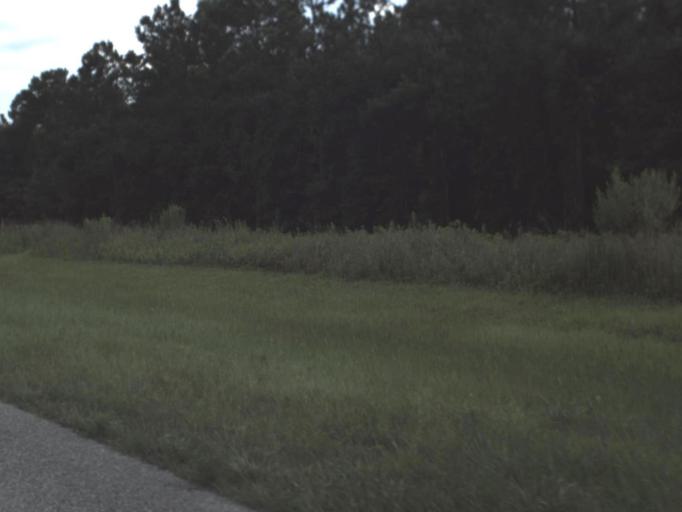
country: US
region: Florida
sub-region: Alachua County
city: Hawthorne
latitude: 29.6435
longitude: -82.1077
